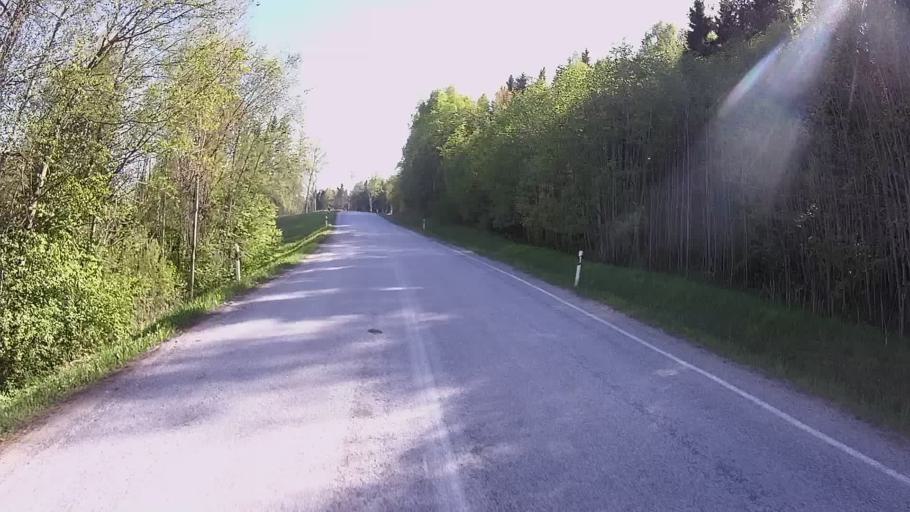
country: EE
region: Vorumaa
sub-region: Antsla vald
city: Vana-Antsla
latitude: 58.0187
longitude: 26.5003
